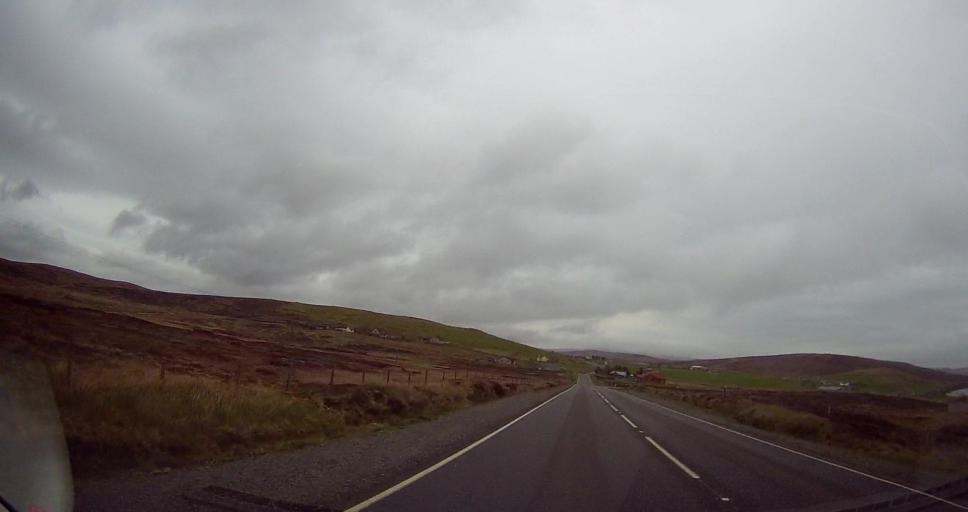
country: GB
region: Scotland
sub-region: Shetland Islands
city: Lerwick
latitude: 60.2318
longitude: -1.2361
